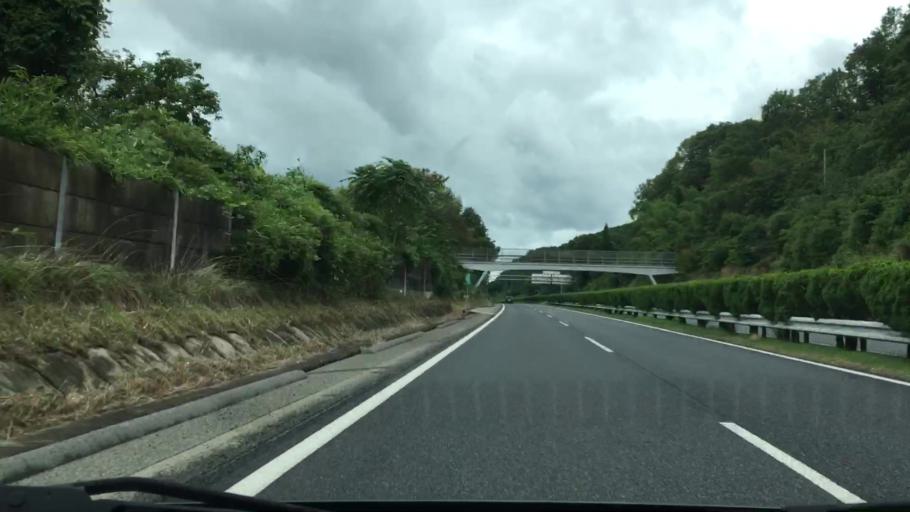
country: JP
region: Okayama
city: Tsuyama
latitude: 35.0400
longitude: 134.1272
